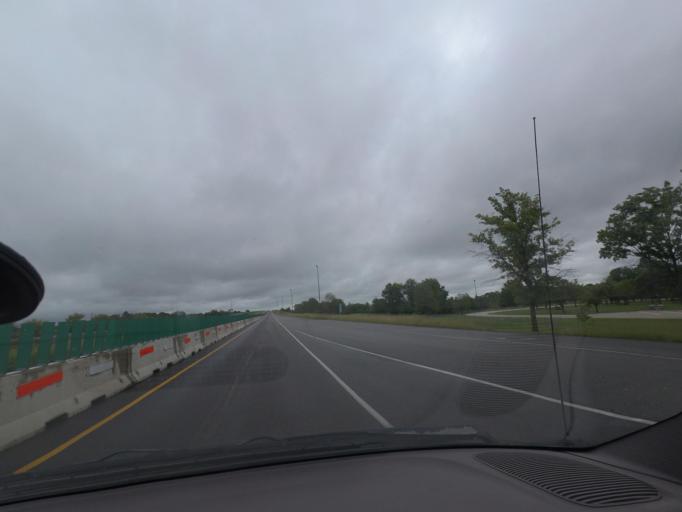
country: US
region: Illinois
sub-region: Piatt County
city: Cerro Gordo
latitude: 39.9926
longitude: -88.7836
